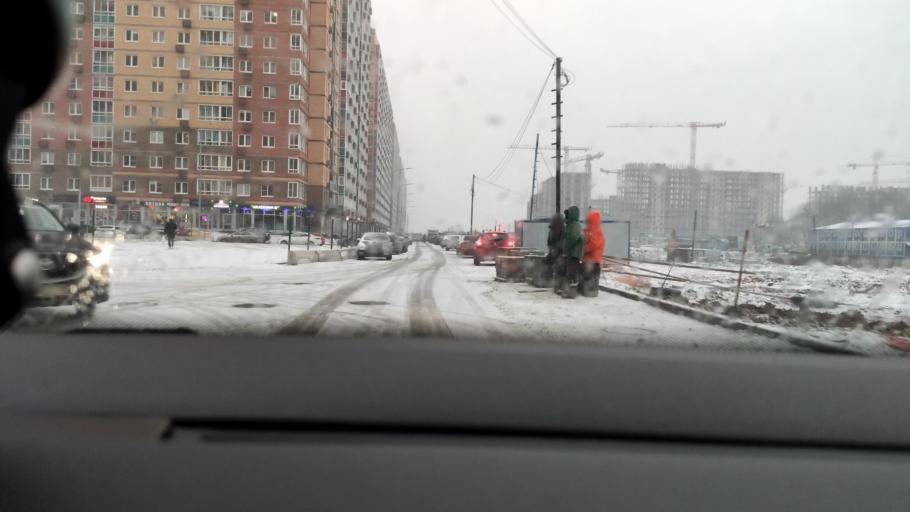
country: RU
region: Moskovskaya
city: Petrovskaya
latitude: 55.5566
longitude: 37.8124
